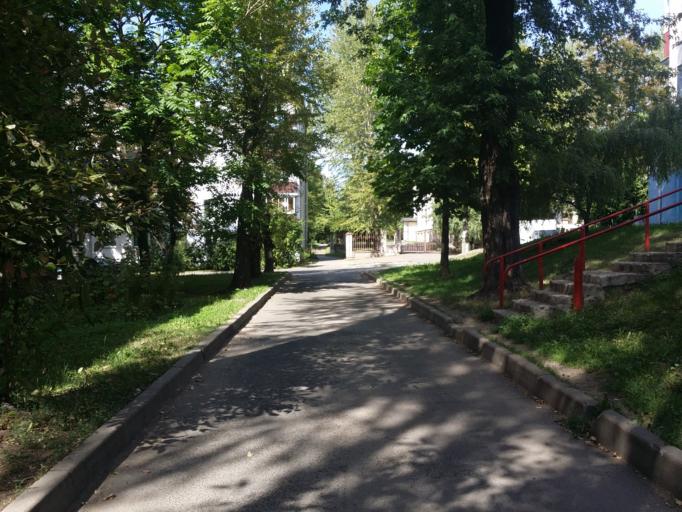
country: BY
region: Minsk
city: Minsk
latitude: 53.8736
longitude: 27.6197
